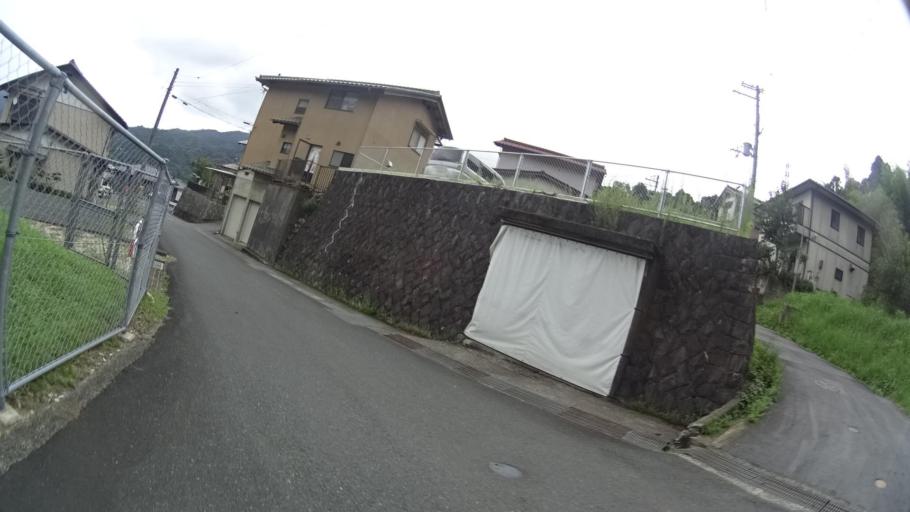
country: JP
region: Kyoto
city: Miyazu
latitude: 35.5273
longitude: 135.1841
